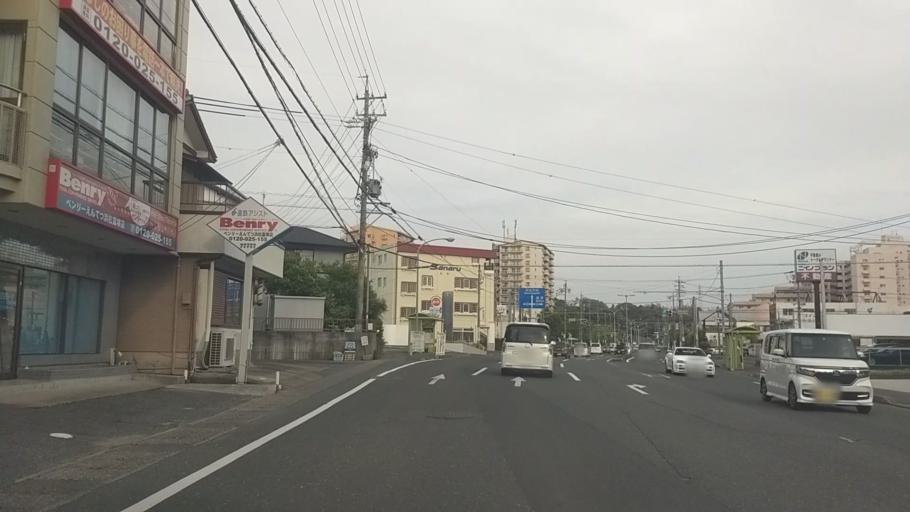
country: JP
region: Shizuoka
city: Hamamatsu
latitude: 34.7240
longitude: 137.6978
